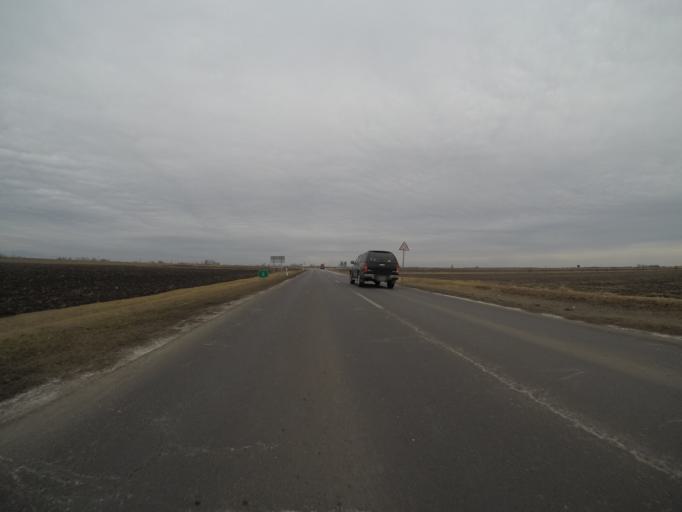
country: HU
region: Jasz-Nagykun-Szolnok
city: Jaszbereny
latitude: 47.5114
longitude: 19.9426
